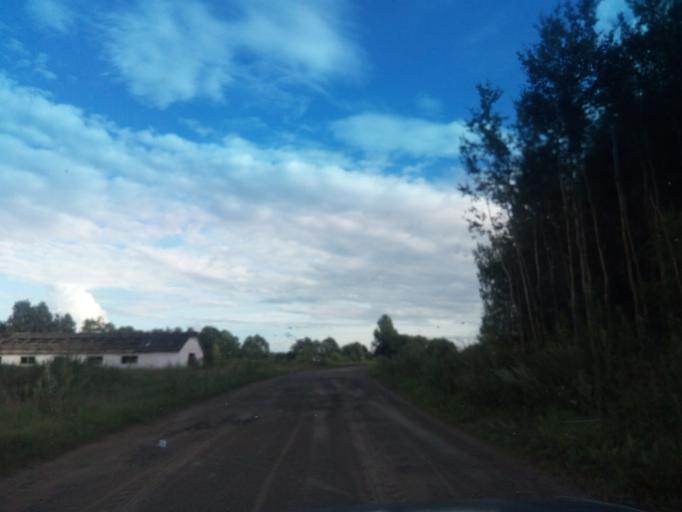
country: BY
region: Vitebsk
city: Dzisna
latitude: 55.6749
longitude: 28.3493
